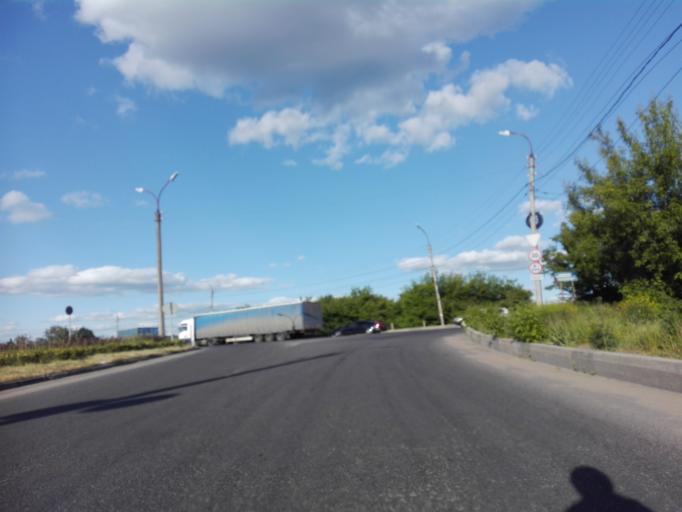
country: RU
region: Orjol
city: Orel
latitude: 52.9395
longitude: 36.0680
